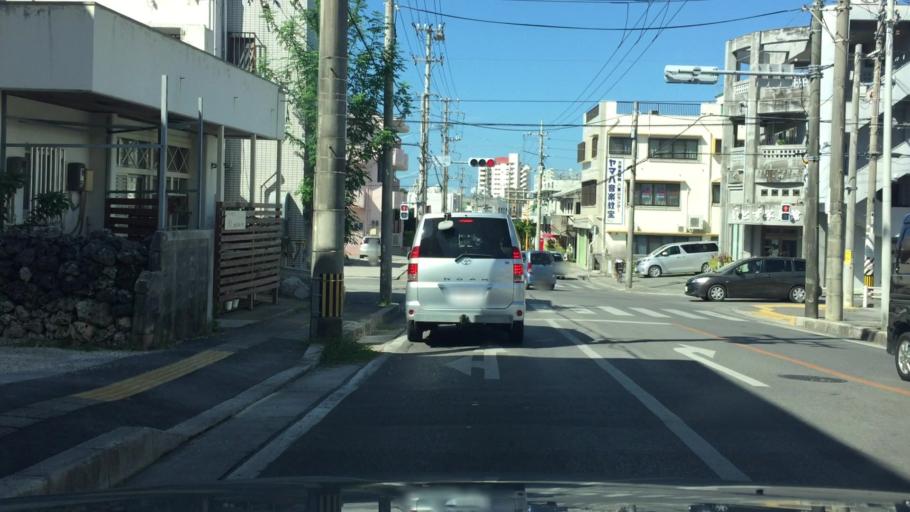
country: JP
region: Okinawa
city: Ishigaki
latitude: 24.3415
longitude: 124.1622
